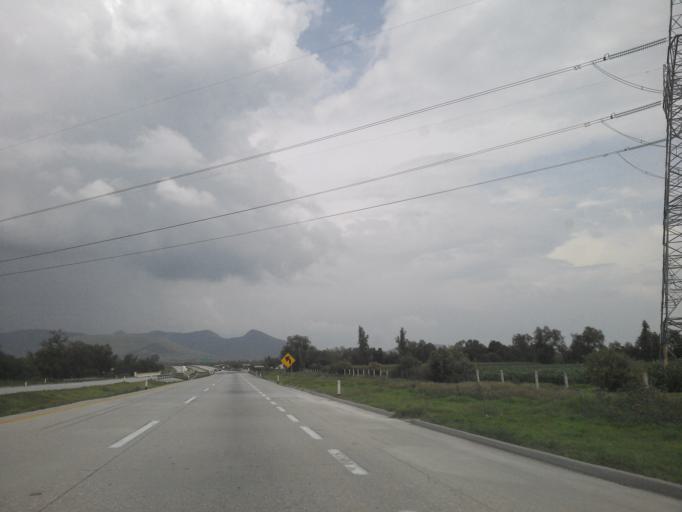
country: MX
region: Hidalgo
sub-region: Atitalaquia
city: Atitalaquia
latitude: 20.0698
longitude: -99.2274
